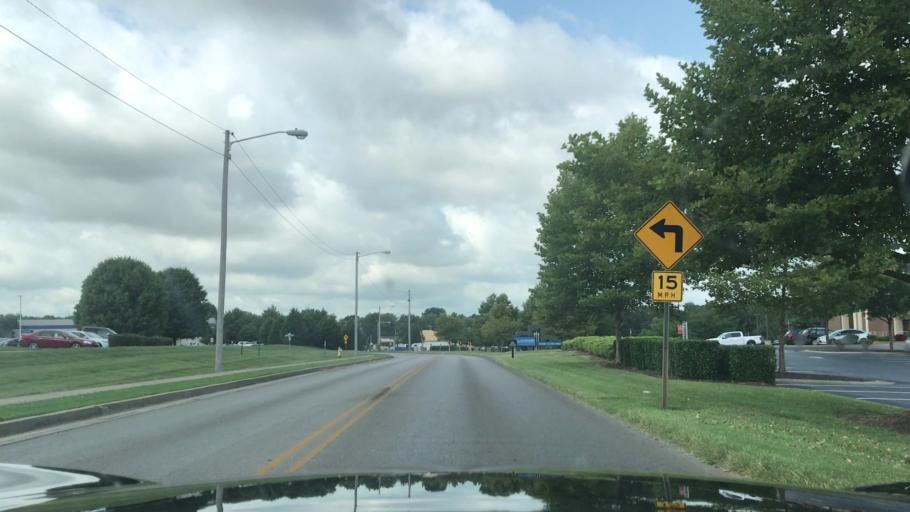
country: US
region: Kentucky
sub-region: Warren County
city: Bowling Green
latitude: 36.9628
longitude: -86.4498
